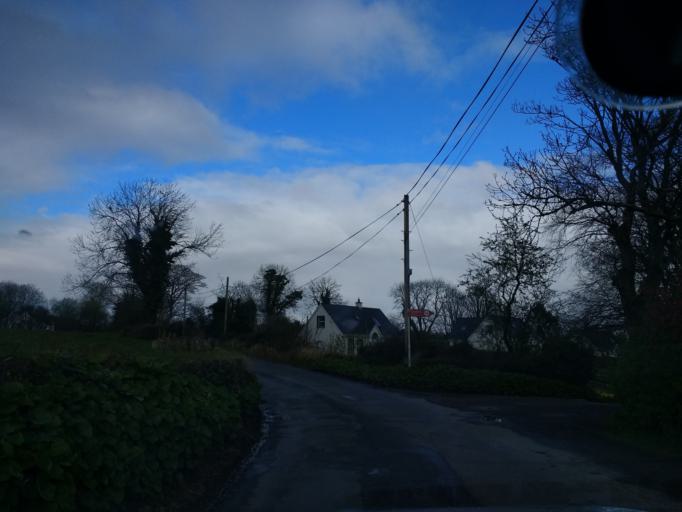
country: IE
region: Ulster
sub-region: County Donegal
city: Buncrana
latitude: 55.1176
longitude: -7.5289
